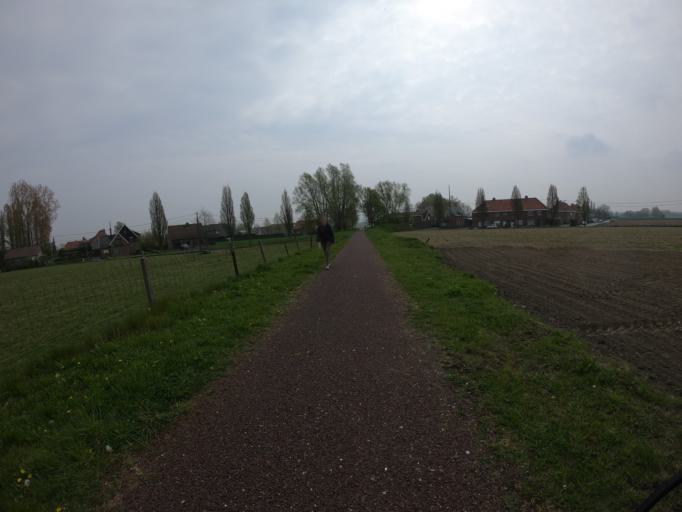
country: BE
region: Flanders
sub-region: Provincie West-Vlaanderen
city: Avelgem
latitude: 50.7774
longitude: 3.4091
